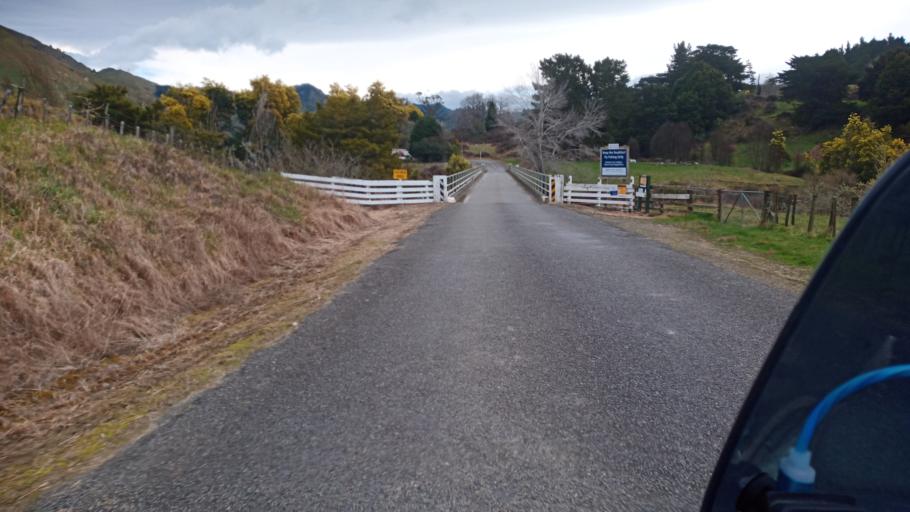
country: NZ
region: Hawke's Bay
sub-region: Wairoa District
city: Wairoa
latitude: -38.7685
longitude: 177.4062
